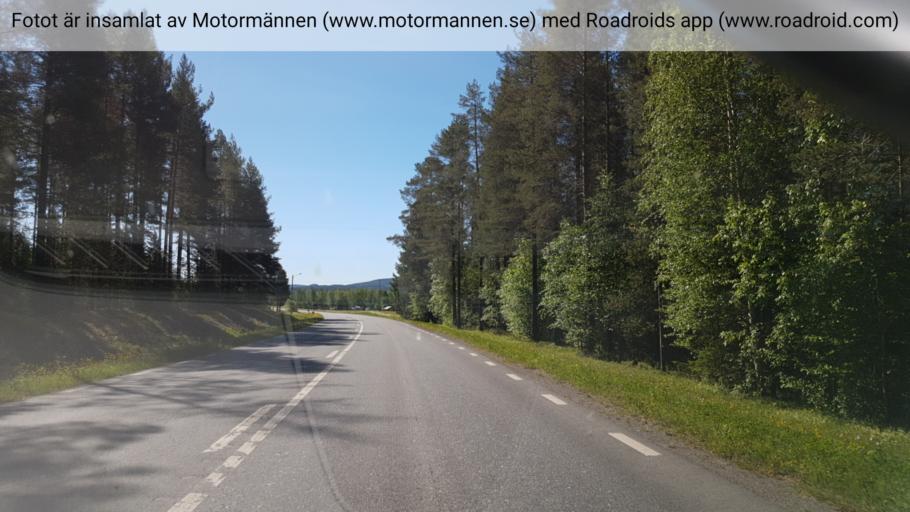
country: SE
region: Norrbotten
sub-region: Bodens Kommun
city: Boden
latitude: 65.8681
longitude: 21.4150
